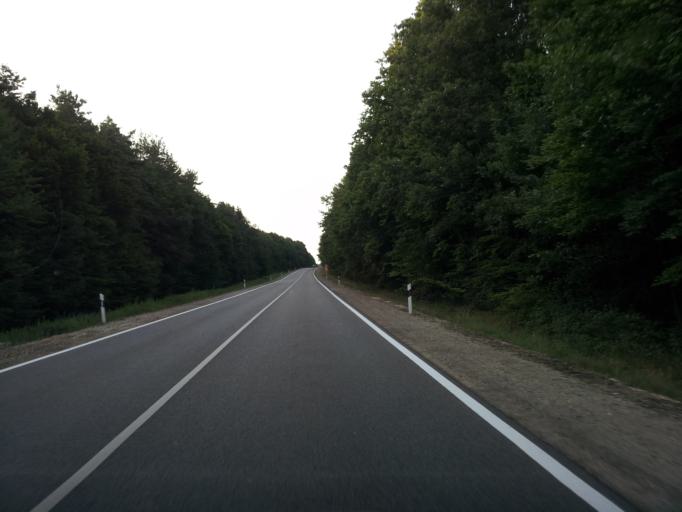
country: HU
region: Zala
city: Zalalovo
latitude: 46.7987
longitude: 16.5632
